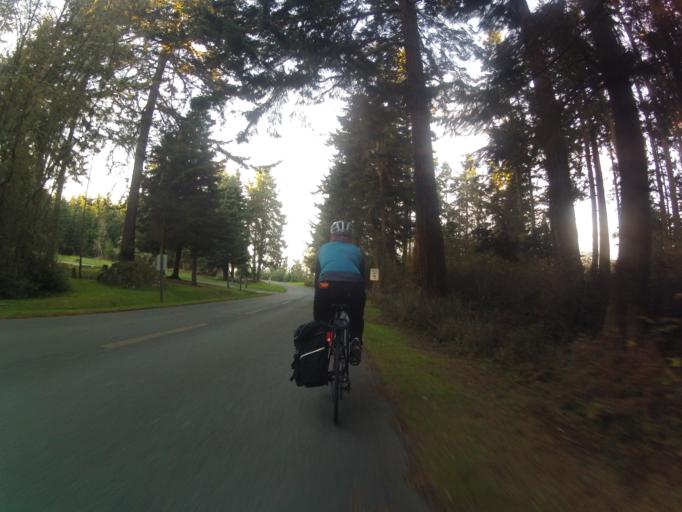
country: US
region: Washington
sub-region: Island County
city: Coupeville
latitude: 48.1599
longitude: -122.6763
